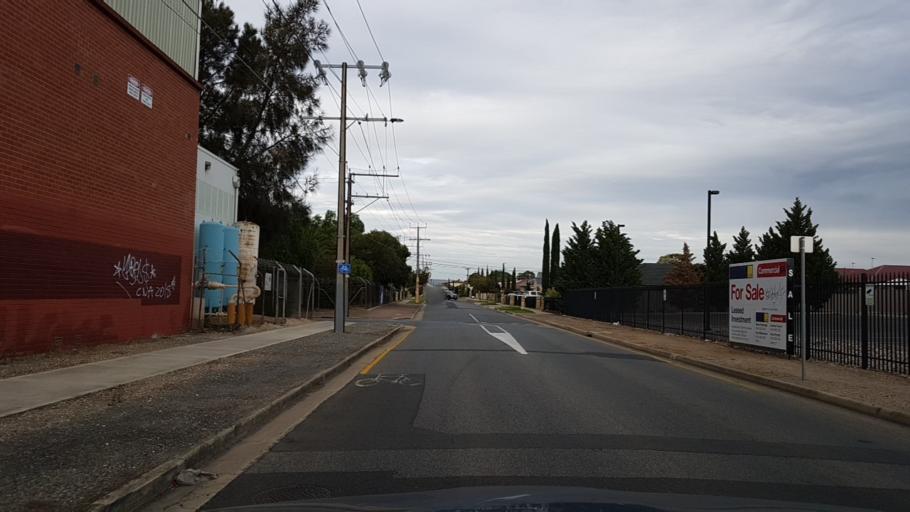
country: AU
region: South Australia
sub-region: Charles Sturt
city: Woodville North
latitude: -34.8598
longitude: 138.5399
